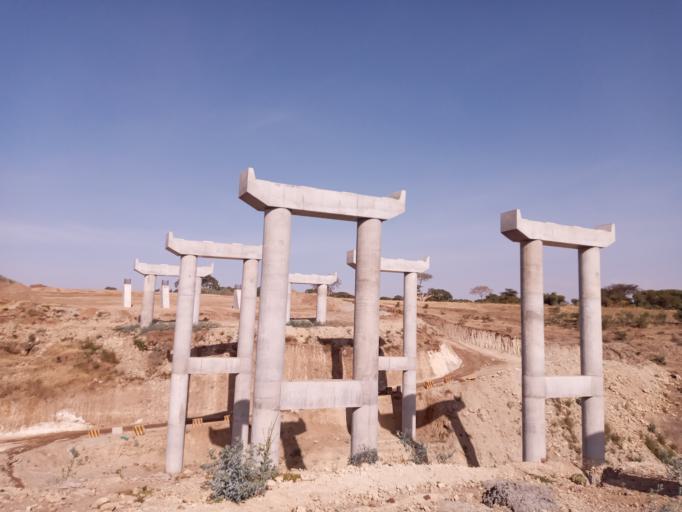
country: ET
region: Oromiya
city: Shashemene
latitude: 7.3146
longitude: 38.6271
